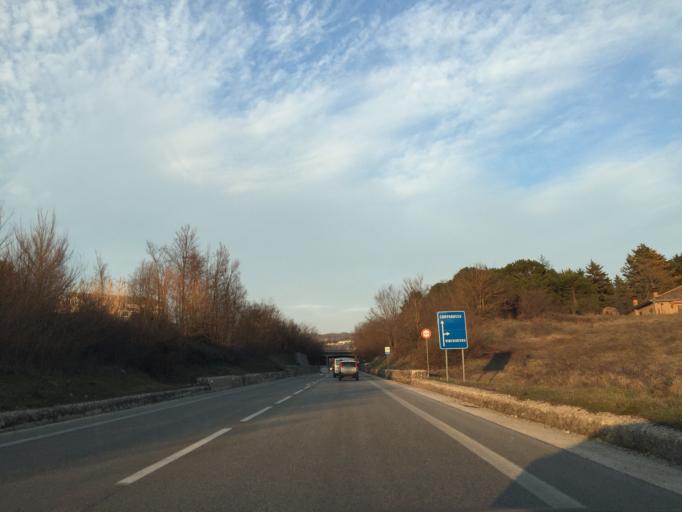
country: IT
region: Molise
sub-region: Provincia di Campobasso
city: Vinchiaturo
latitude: 41.4900
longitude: 14.5994
